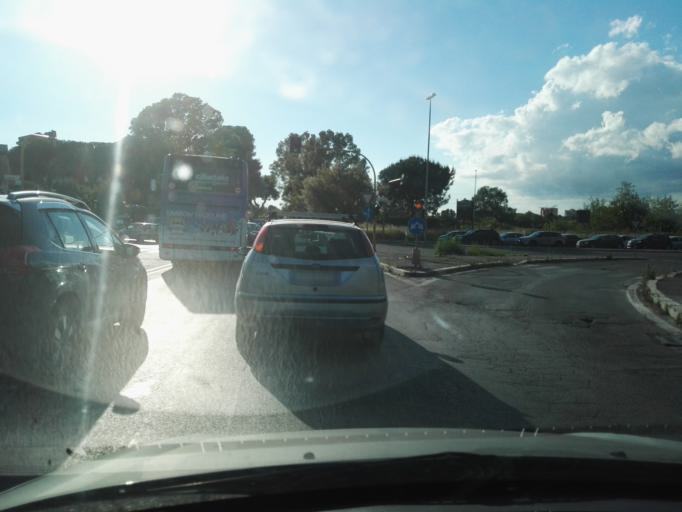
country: IT
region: Latium
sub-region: Citta metropolitana di Roma Capitale
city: Selcetta
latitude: 41.8011
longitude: 12.4817
